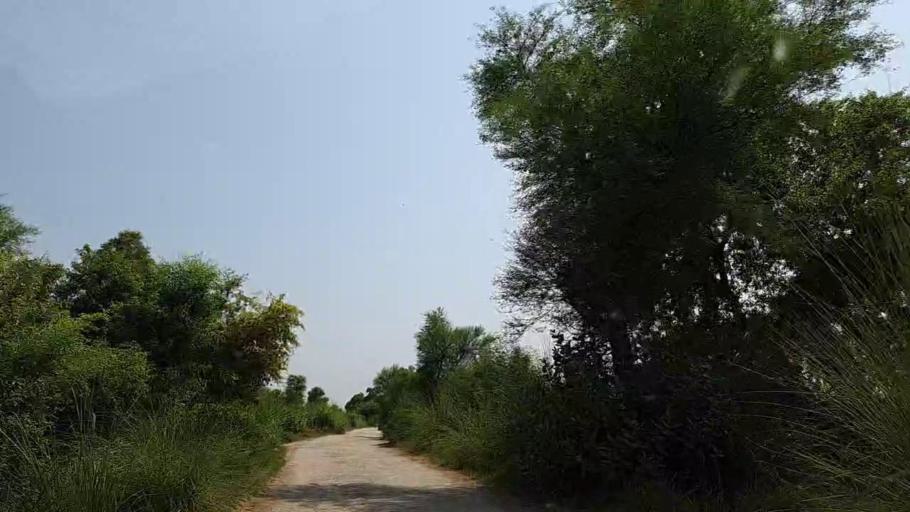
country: PK
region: Sindh
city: Adilpur
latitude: 27.9063
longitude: 69.3632
